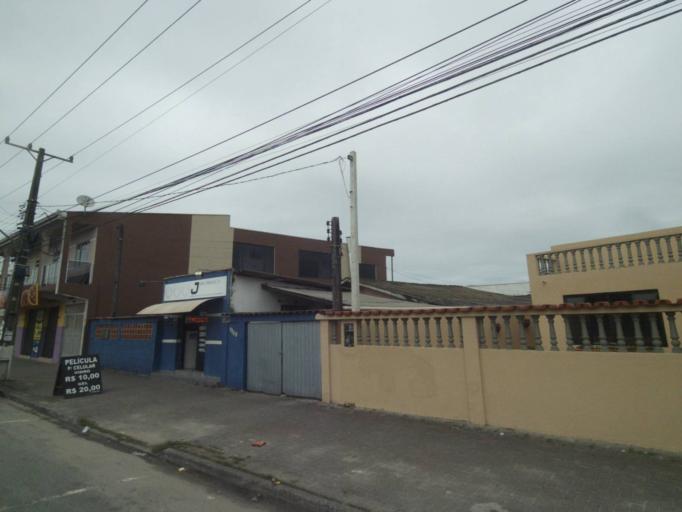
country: BR
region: Parana
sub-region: Paranagua
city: Paranagua
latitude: -25.5207
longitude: -48.5345
